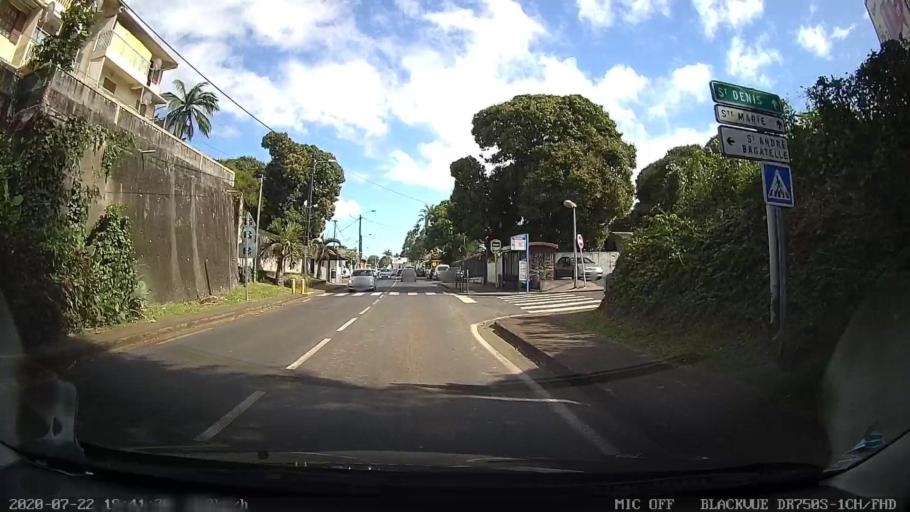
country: RE
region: Reunion
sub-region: Reunion
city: Sainte-Suzanne
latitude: -20.9036
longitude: 55.6021
